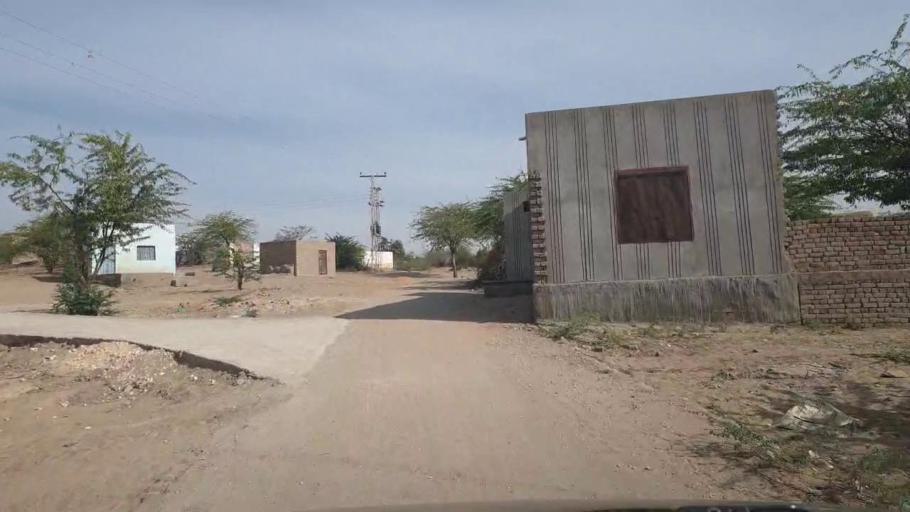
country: PK
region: Sindh
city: Umarkot
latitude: 25.2987
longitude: 69.7225
